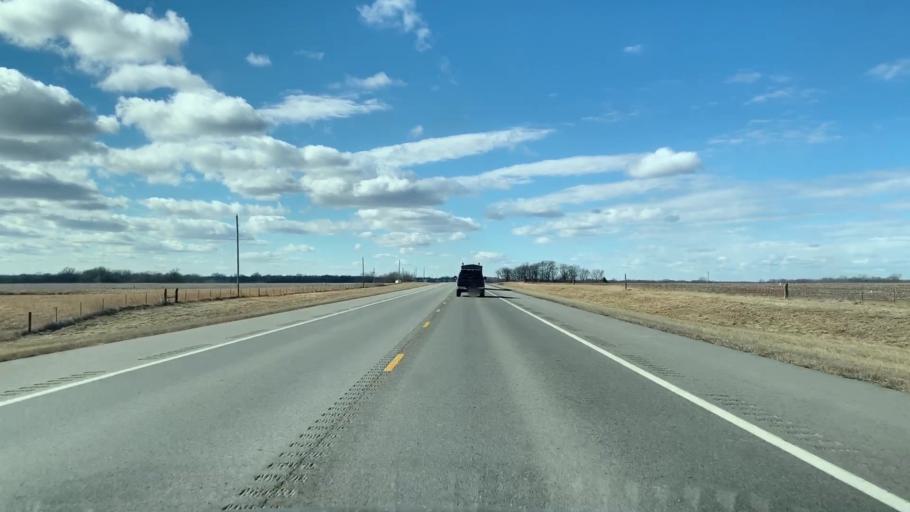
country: US
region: Kansas
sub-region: Cherokee County
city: Columbus
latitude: 37.3397
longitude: -94.8631
